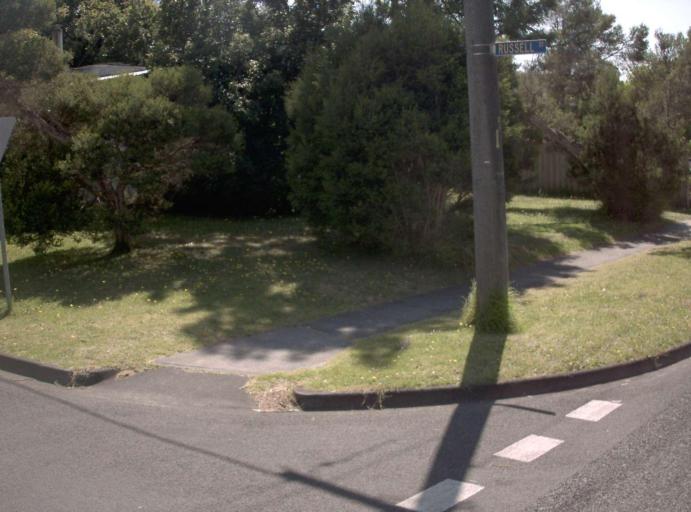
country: AU
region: Victoria
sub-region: Bass Coast
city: North Wonthaggi
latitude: -38.6316
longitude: 145.7313
